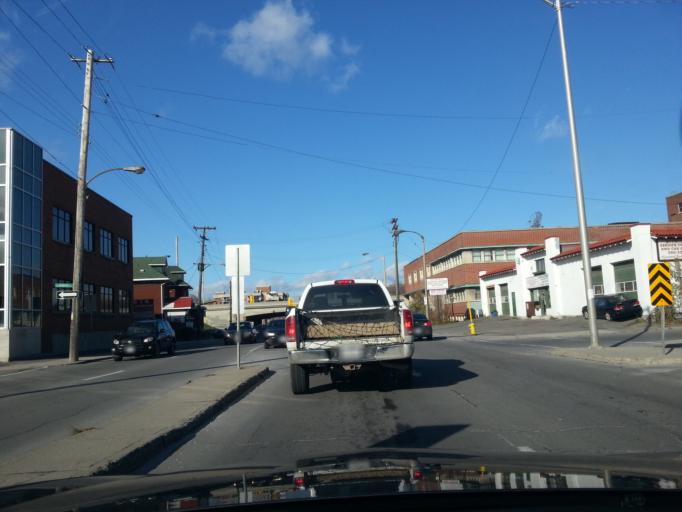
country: CA
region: Ontario
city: Ottawa
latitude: 45.4038
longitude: -75.7012
